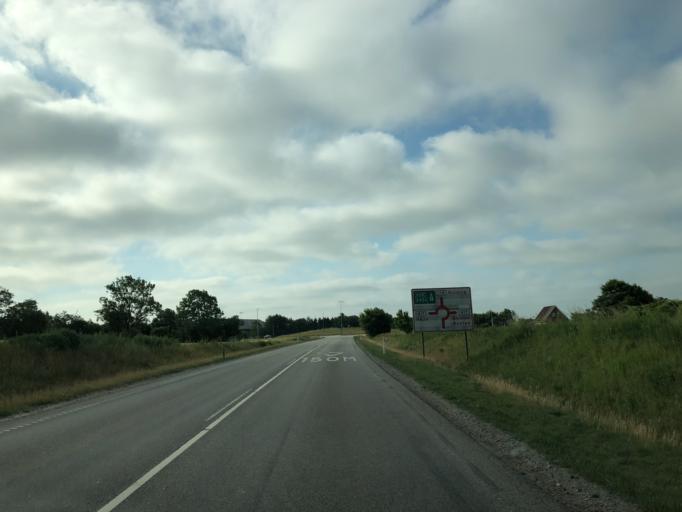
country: DK
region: South Denmark
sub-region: Vejle Kommune
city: Jelling
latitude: 55.6659
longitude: 9.4071
